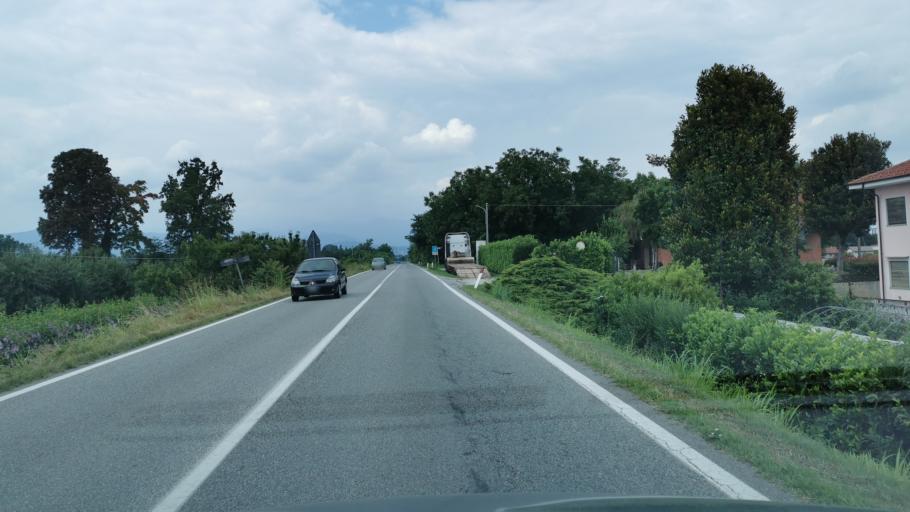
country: IT
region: Piedmont
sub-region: Provincia di Torino
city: Garzigliana
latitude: 44.8243
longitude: 7.3698
